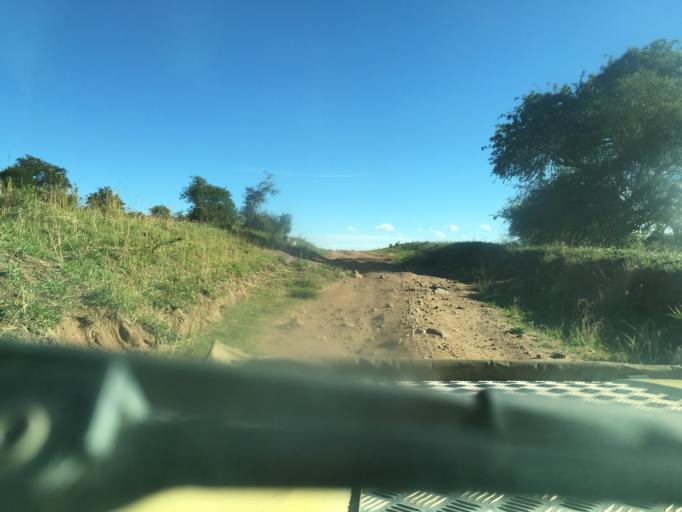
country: TZ
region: Mara
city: Mugumu
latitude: -1.9997
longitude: 35.1656
